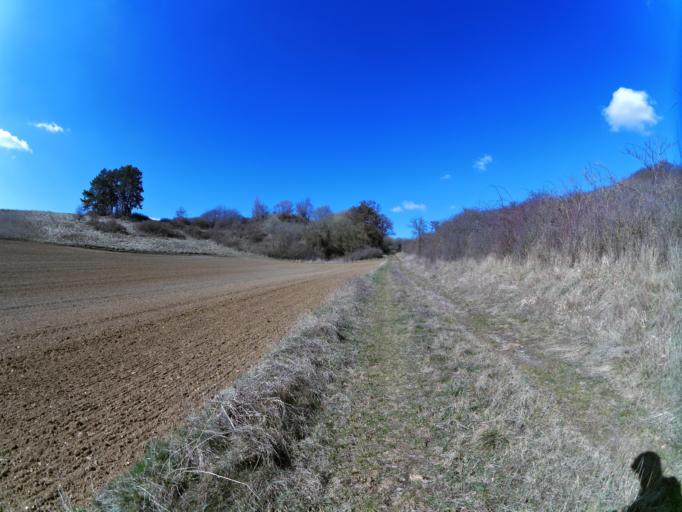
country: DE
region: Bavaria
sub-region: Regierungsbezirk Unterfranken
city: Greussenheim
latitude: 49.7982
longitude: 9.7795
